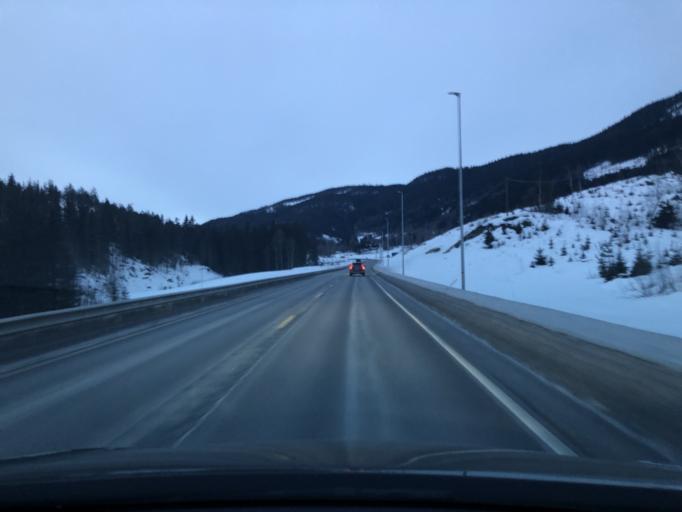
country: NO
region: Oppland
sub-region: Sor-Aurdal
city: Bagn
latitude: 60.8857
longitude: 9.4822
